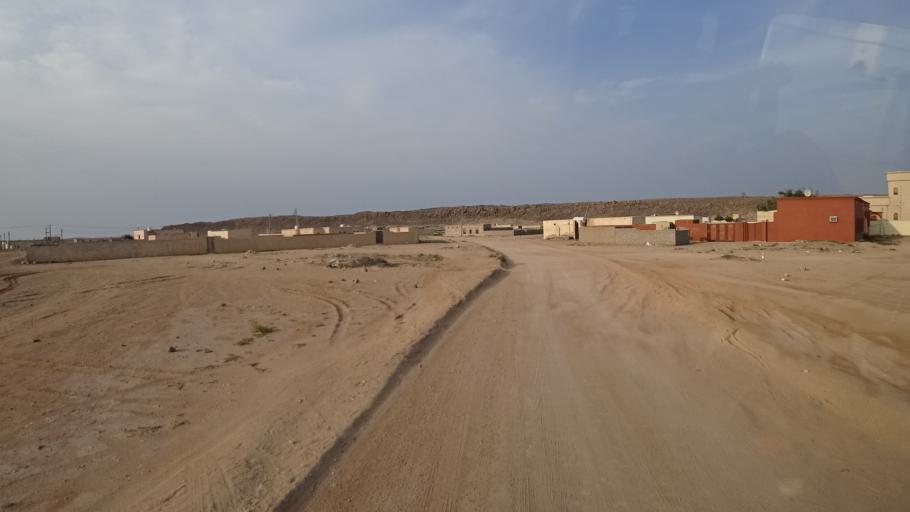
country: OM
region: Ash Sharqiyah
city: Sur
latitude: 22.4352
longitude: 59.8266
